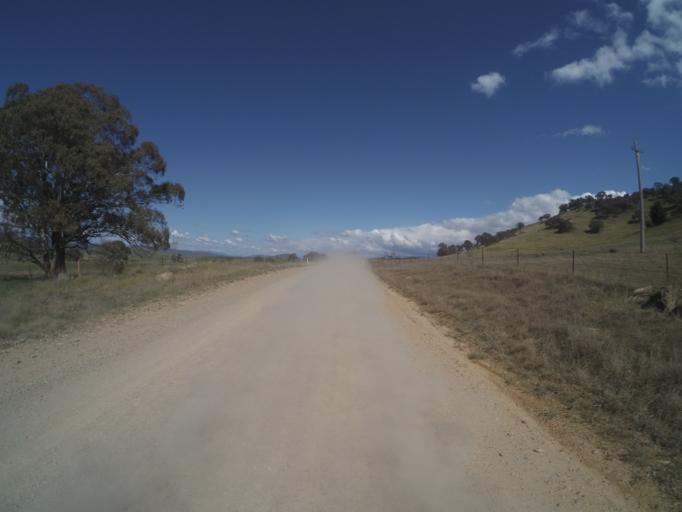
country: AU
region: Australian Capital Territory
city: Macquarie
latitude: -35.2346
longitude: 148.9124
